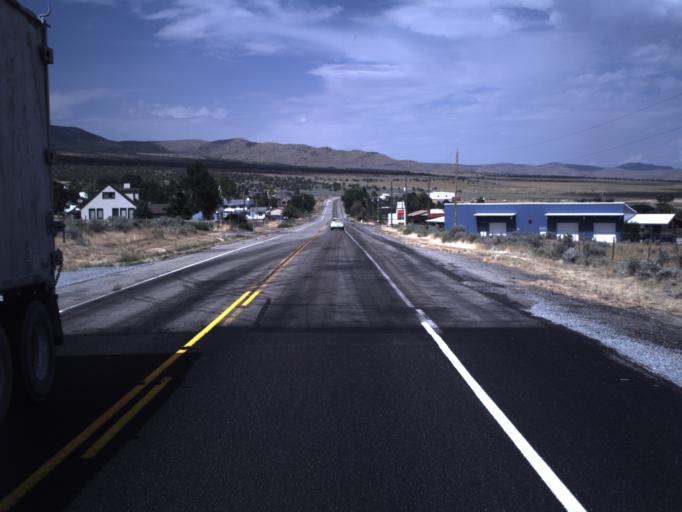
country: US
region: Utah
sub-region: Utah County
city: Eagle Mountain
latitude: 40.3226
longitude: -112.1024
